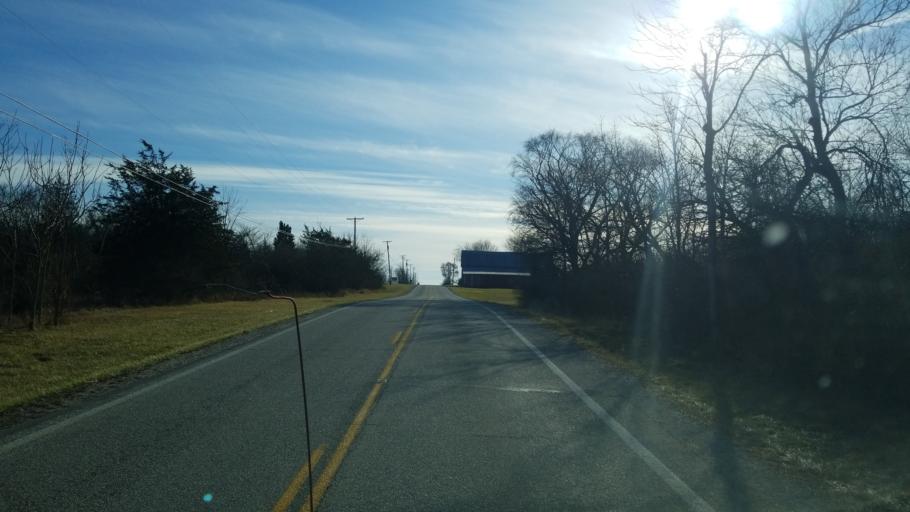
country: US
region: Ohio
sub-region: Sandusky County
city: Stony Prairie
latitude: 41.3811
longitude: -83.2224
